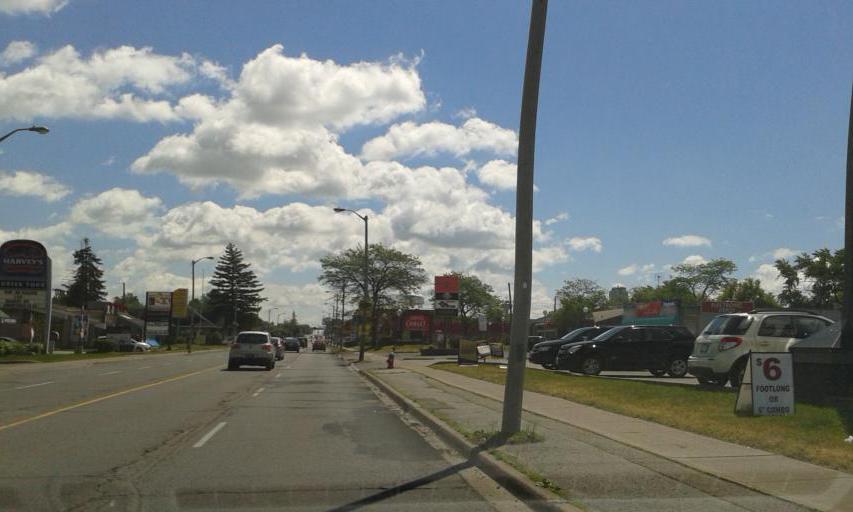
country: CA
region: Ontario
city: Niagara Falls
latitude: 43.0892
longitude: -79.1080
